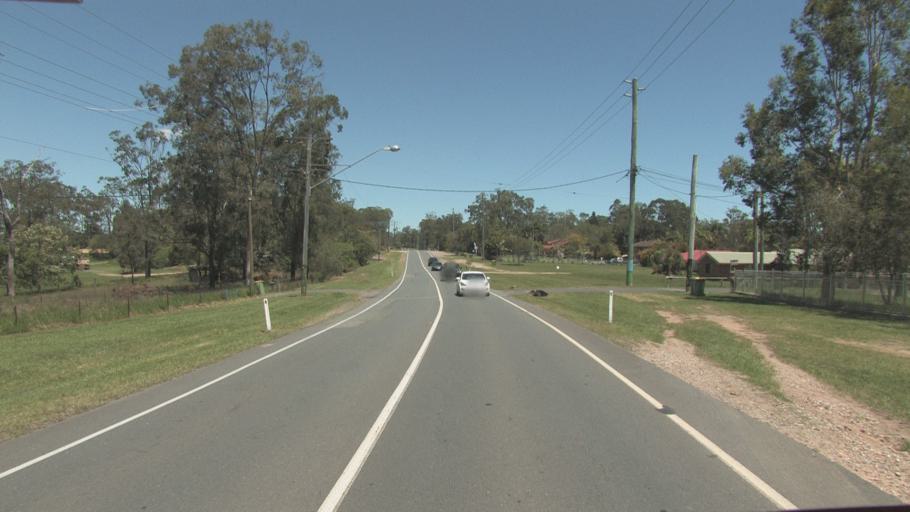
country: AU
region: Queensland
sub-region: Logan
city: Park Ridge South
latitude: -27.7049
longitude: 153.0065
